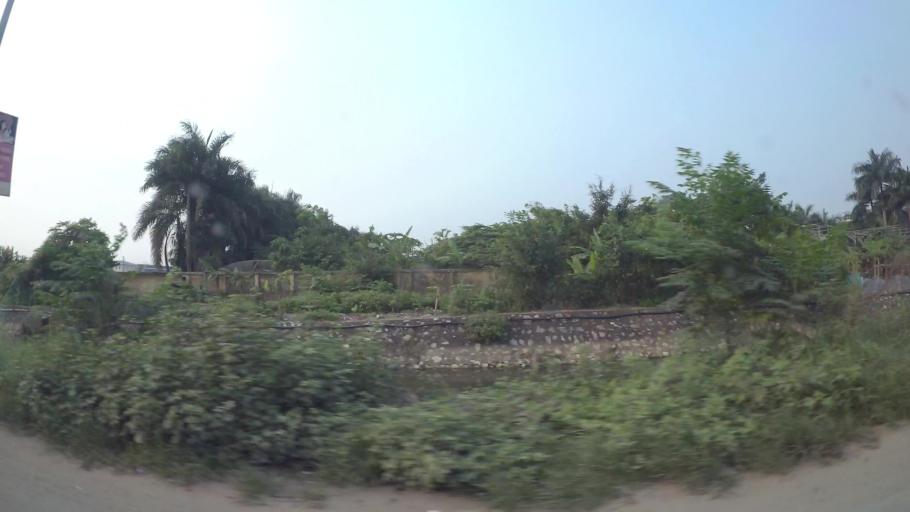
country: VN
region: Ha Noi
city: Thuong Tin
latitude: 20.8710
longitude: 105.8750
